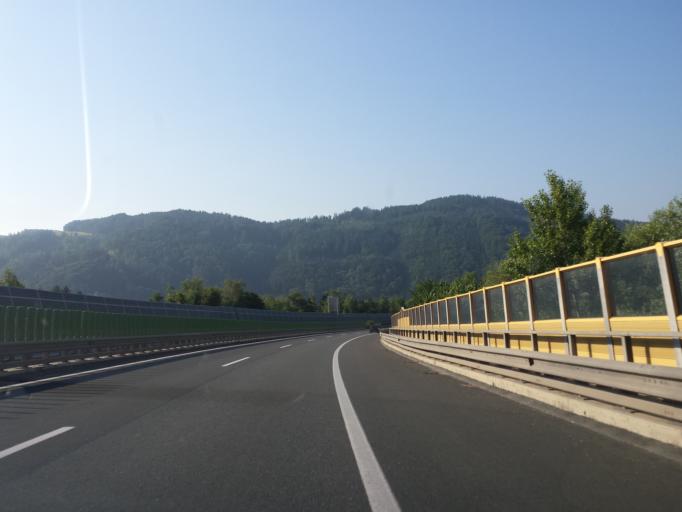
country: AT
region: Styria
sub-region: Politischer Bezirk Graz-Umgebung
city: Peggau
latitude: 47.2005
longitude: 15.3447
